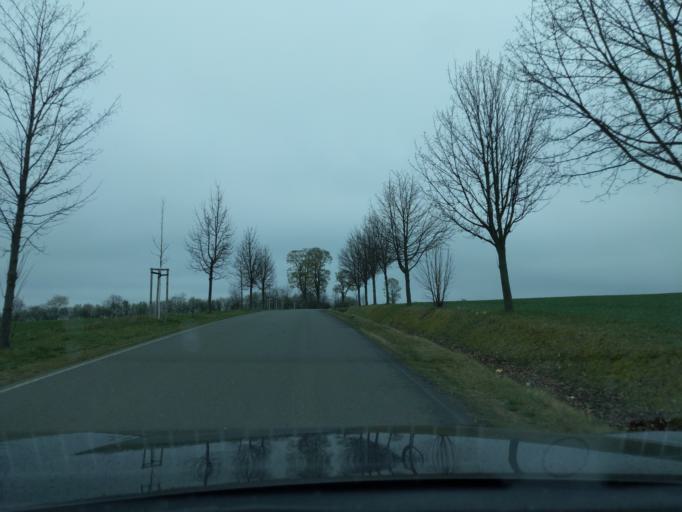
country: DE
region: Saxony
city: Zschorlau
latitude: 50.5804
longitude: 12.6457
